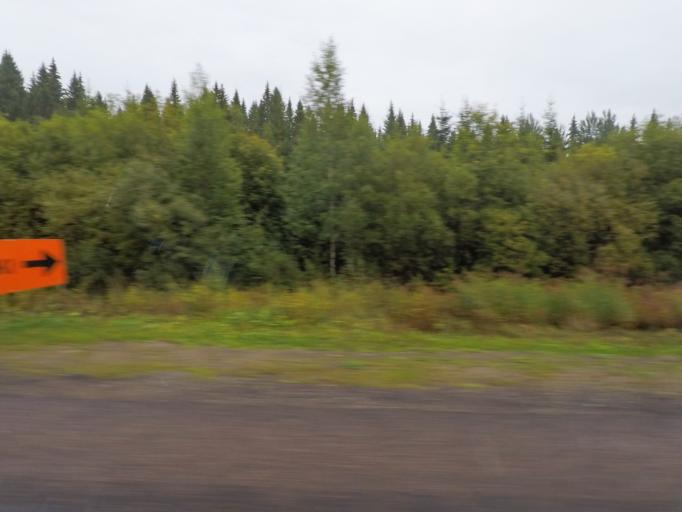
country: FI
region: Northern Savo
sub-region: Varkaus
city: Leppaevirta
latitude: 62.4402
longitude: 27.8047
